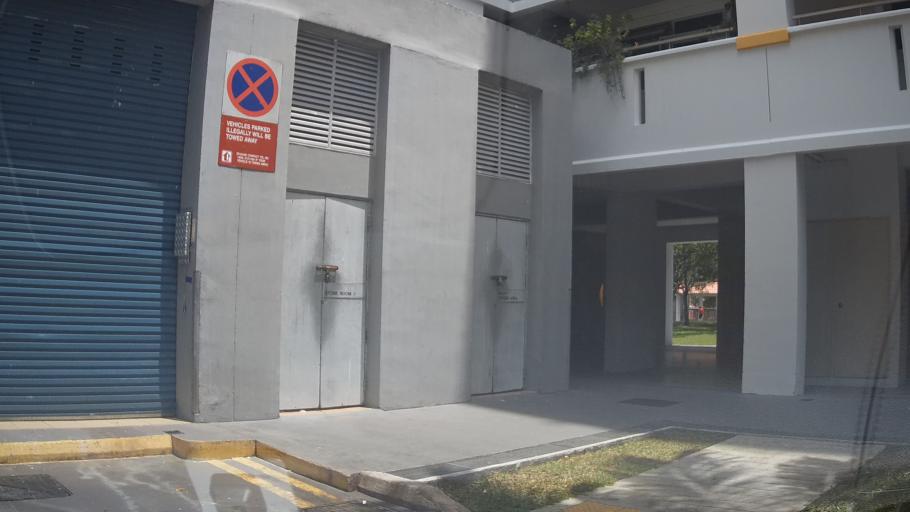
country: MY
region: Johor
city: Kampung Pasir Gudang Baru
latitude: 1.3773
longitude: 103.9342
